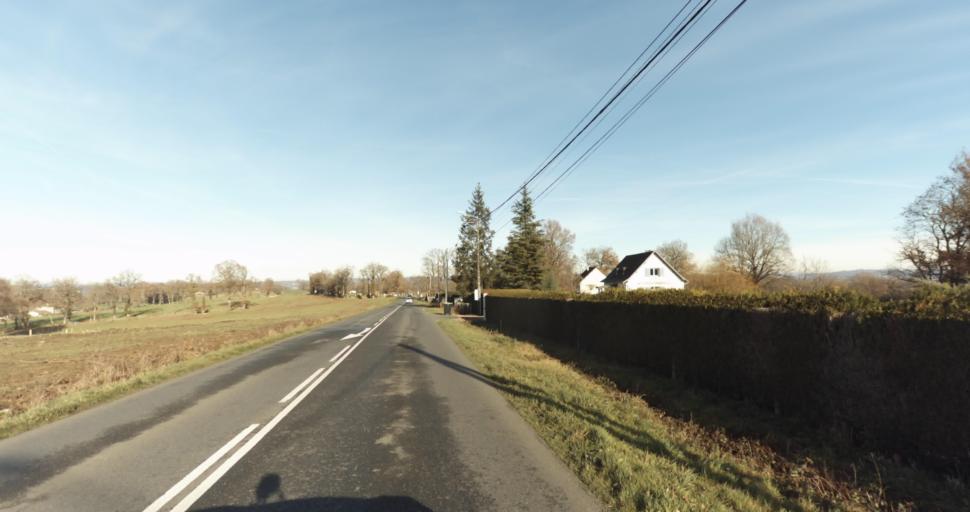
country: FR
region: Limousin
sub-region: Departement de la Haute-Vienne
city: Aixe-sur-Vienne
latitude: 45.7803
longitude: 1.1187
